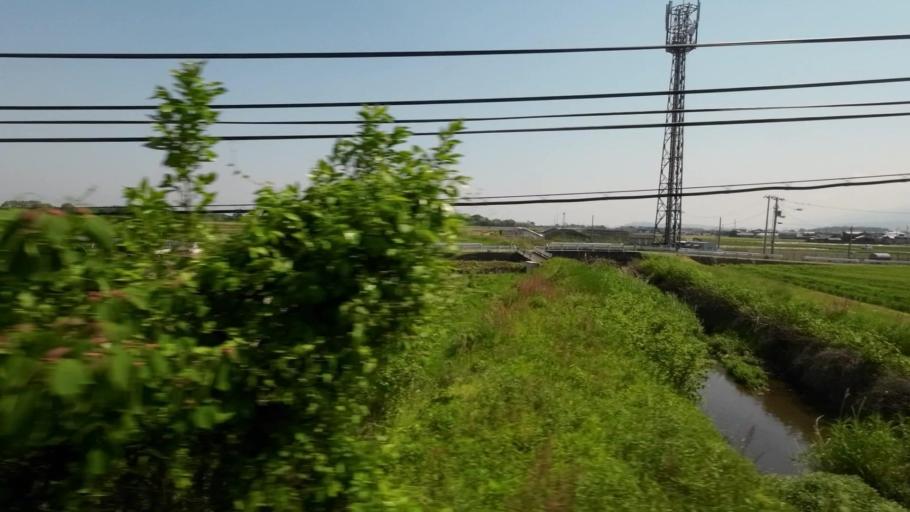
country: JP
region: Ehime
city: Saijo
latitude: 33.9002
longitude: 133.1009
